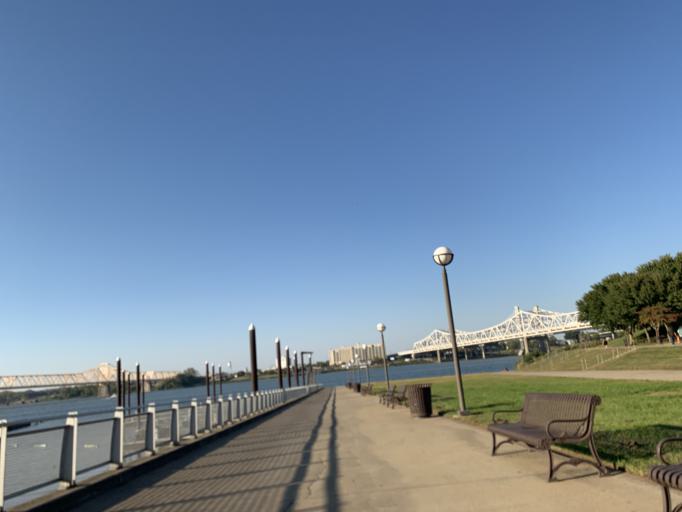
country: US
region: Kentucky
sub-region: Jefferson County
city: Louisville
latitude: 38.2605
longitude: -85.7463
